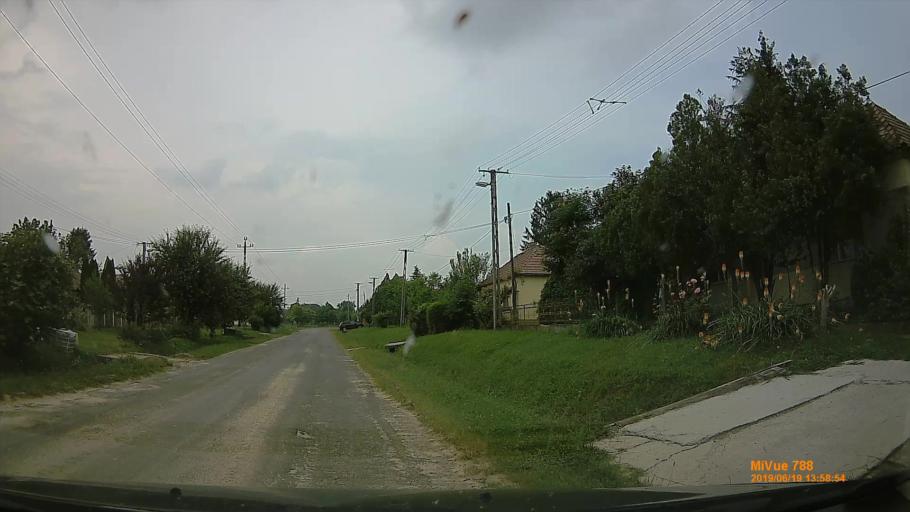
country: HU
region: Baranya
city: Szigetvar
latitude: 46.0883
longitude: 17.7979
